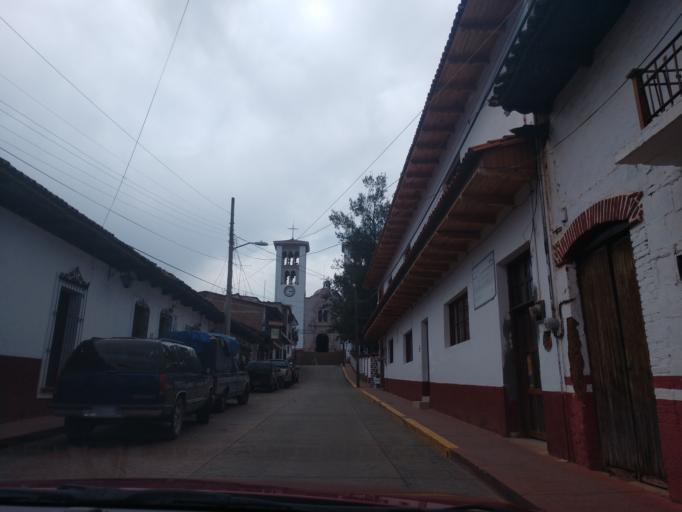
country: MX
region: Jalisco
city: La Manzanilla de la Paz
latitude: 20.0054
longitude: -103.1546
